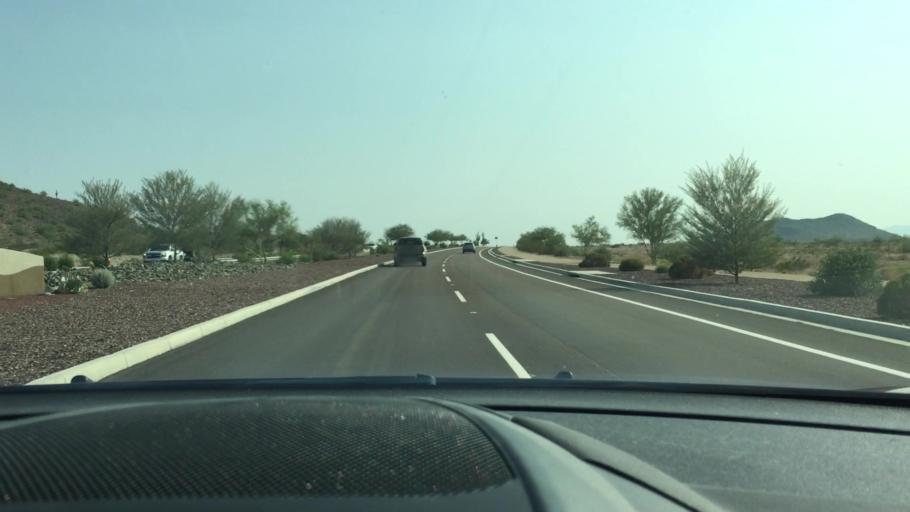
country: US
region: Arizona
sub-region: Maricopa County
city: Sun City West
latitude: 33.7502
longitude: -112.2542
